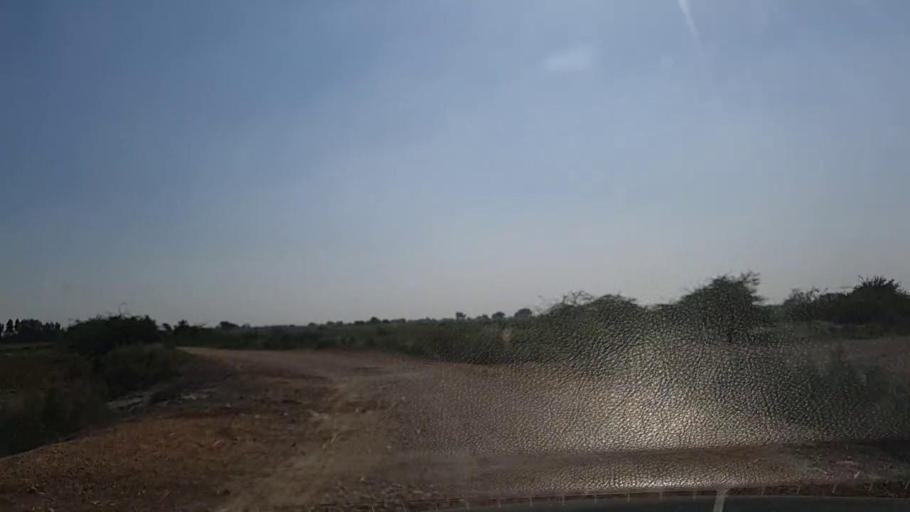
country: PK
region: Sindh
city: Daro Mehar
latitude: 24.7590
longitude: 68.0623
